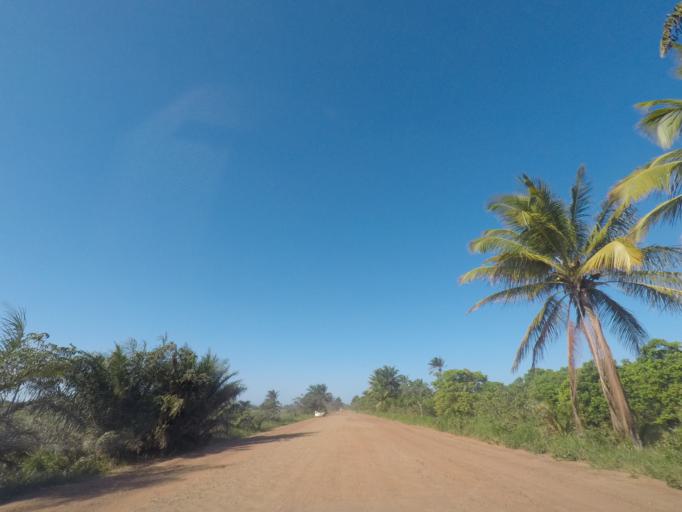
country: BR
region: Bahia
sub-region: Marau
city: Marau
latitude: -14.0558
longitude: -38.9561
